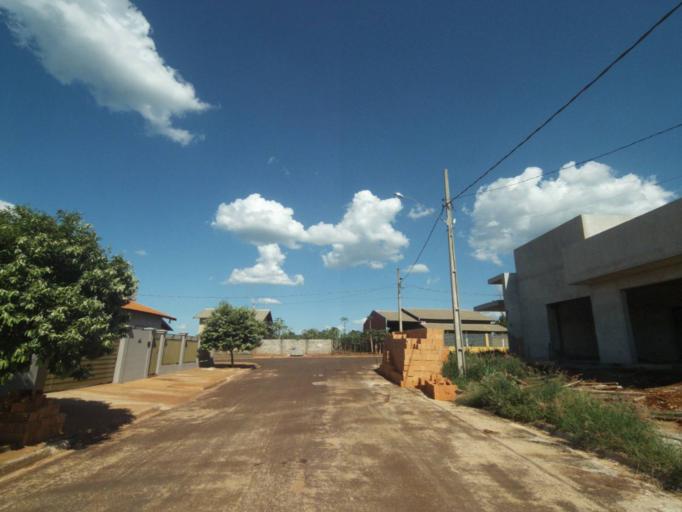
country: BR
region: Parana
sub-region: Sertanopolis
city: Sertanopolis
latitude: -23.0377
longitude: -50.8105
